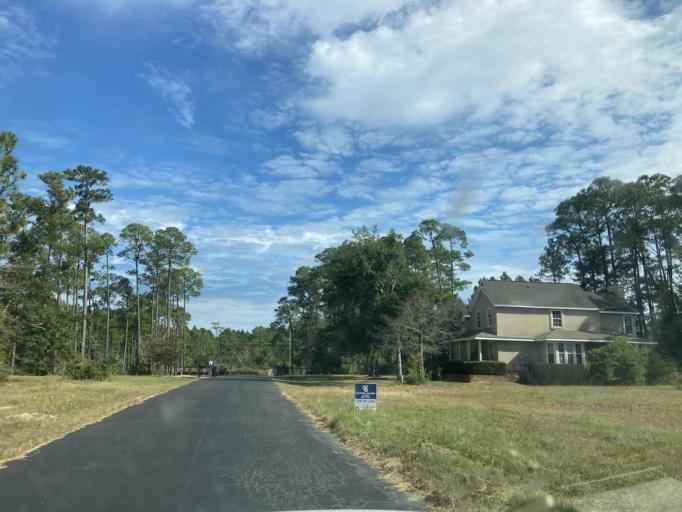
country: US
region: Mississippi
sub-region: Jackson County
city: Saint Martin
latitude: 30.4344
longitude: -88.8629
